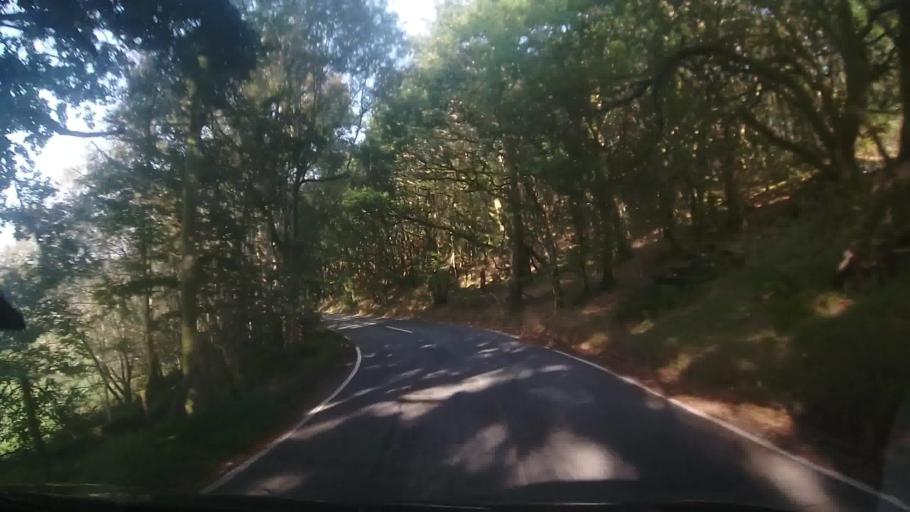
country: GB
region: Wales
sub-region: County of Ceredigion
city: Lledrod
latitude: 52.3450
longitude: -3.8463
